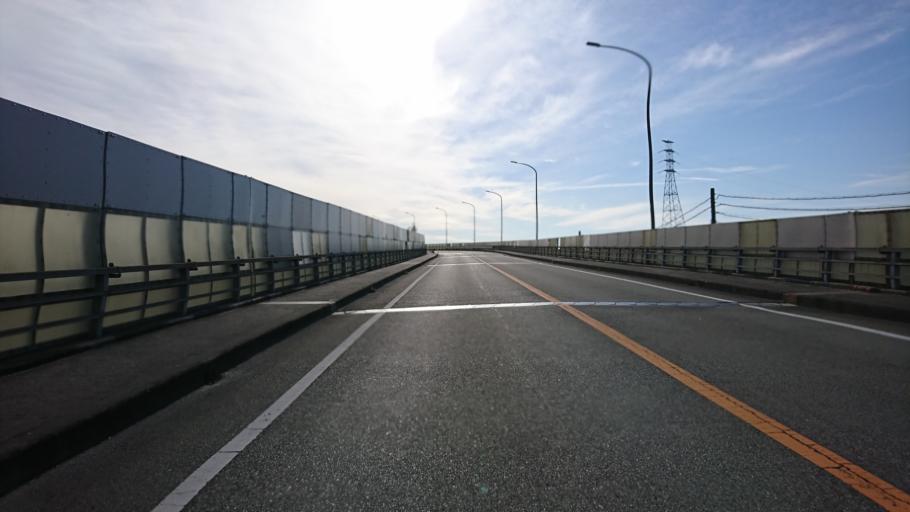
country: JP
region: Hyogo
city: Kakogawacho-honmachi
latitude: 34.7417
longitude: 134.8018
